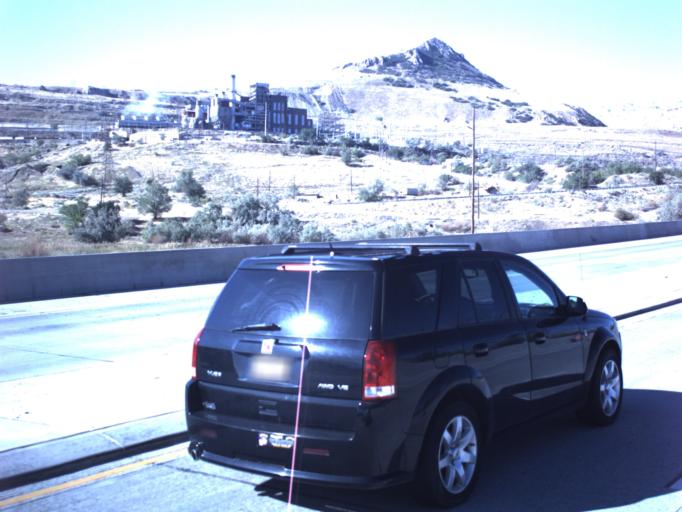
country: US
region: Utah
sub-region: Salt Lake County
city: Magna
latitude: 40.7182
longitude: -112.1148
